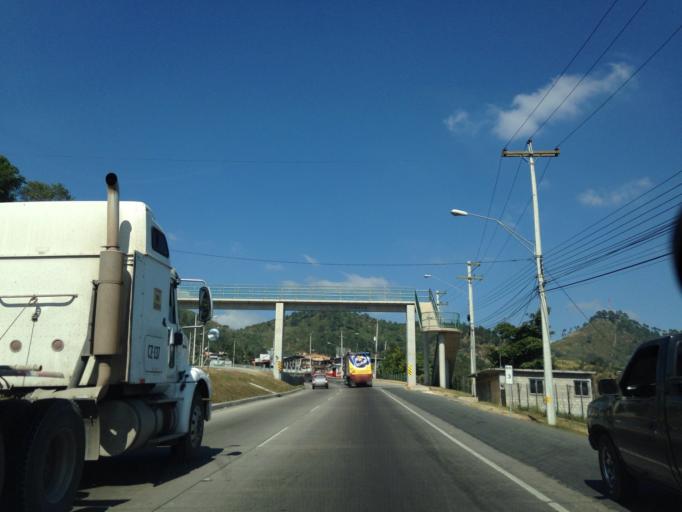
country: HN
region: Francisco Morazan
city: El Lolo
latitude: 14.1221
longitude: -87.2609
